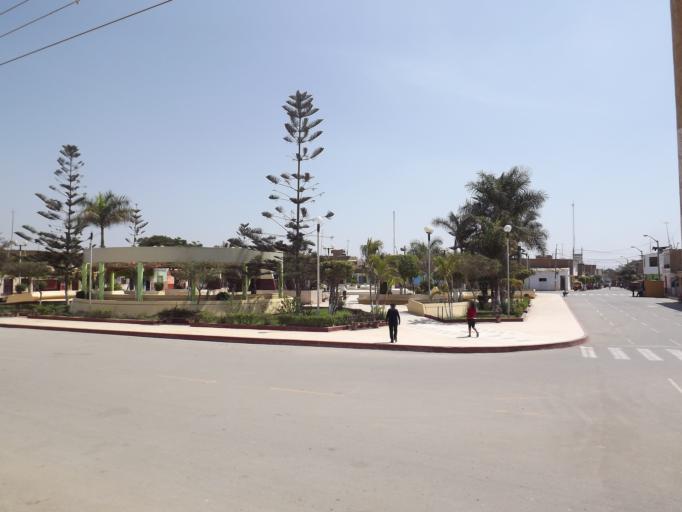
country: PE
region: Lambayeque
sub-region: Provincia de Lambayeque
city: Tucume
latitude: -6.4744
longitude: -79.8550
